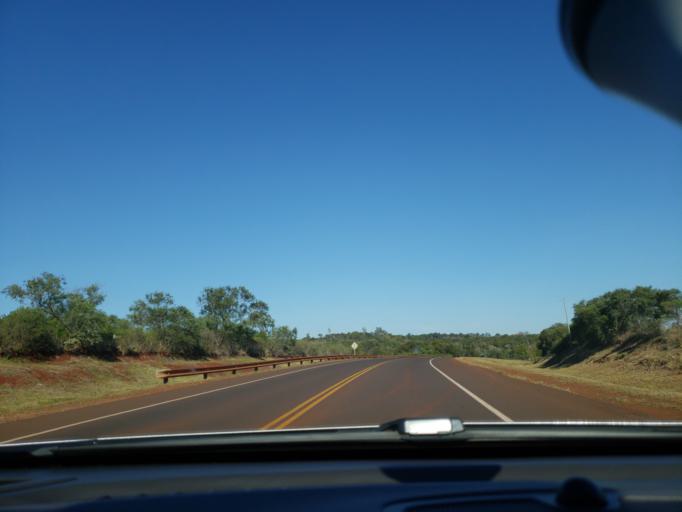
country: AR
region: Misiones
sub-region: Departamento de Apostoles
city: Apostoles
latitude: -27.8511
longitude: -55.7635
